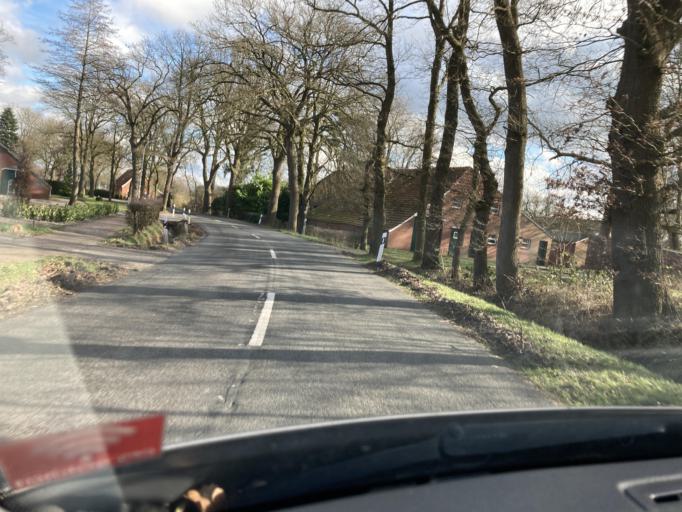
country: DE
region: Lower Saxony
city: Detern
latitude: 53.2499
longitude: 7.6838
